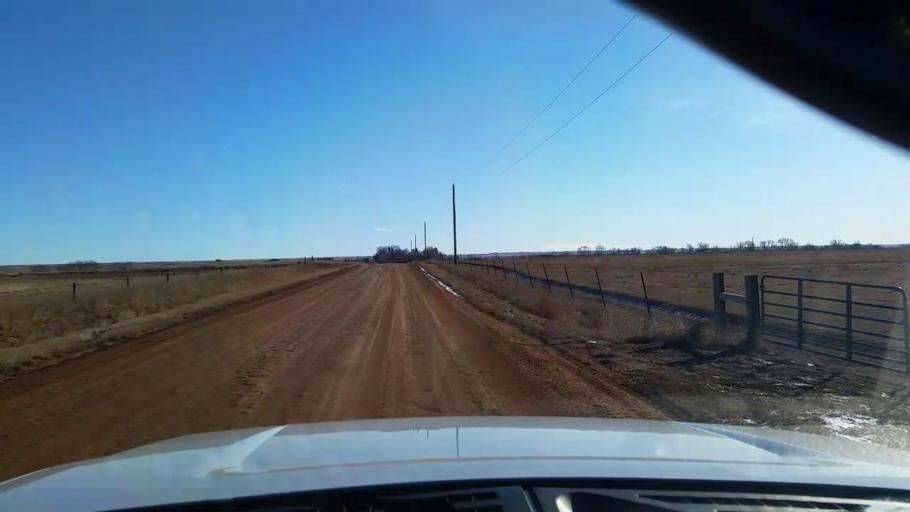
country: US
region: Colorado
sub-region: Larimer County
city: Wellington
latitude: 40.7693
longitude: -105.0602
